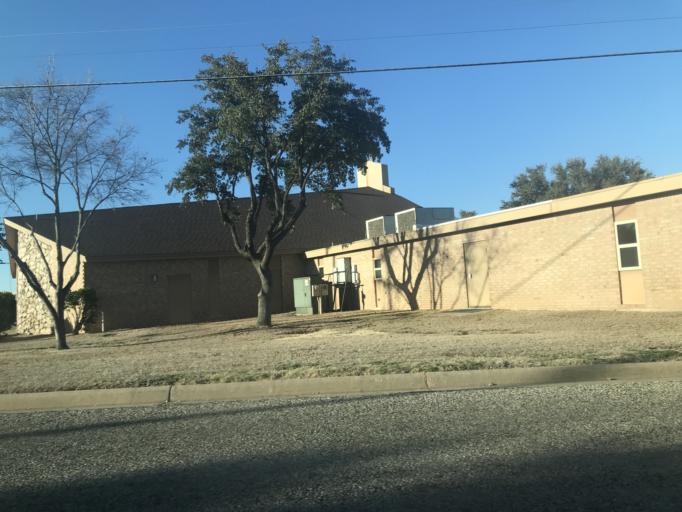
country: US
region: Texas
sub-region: Tom Green County
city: San Angelo
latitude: 31.4421
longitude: -100.4810
